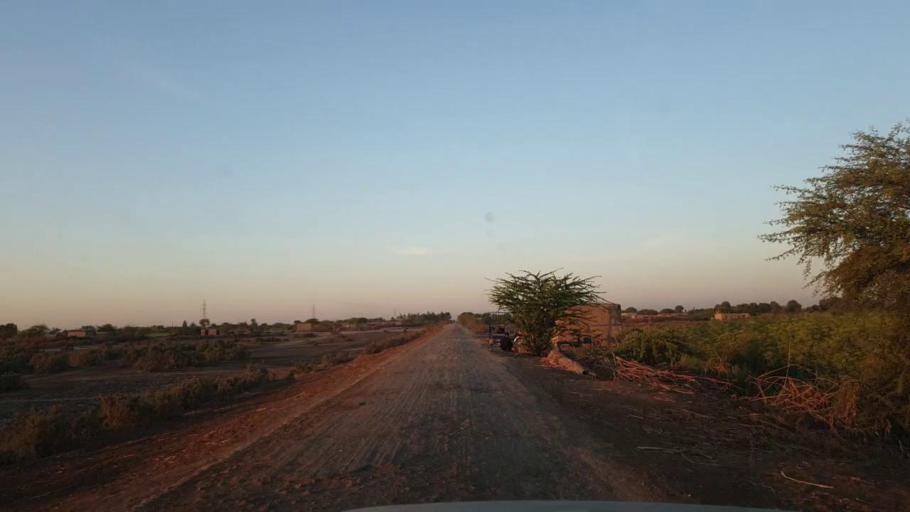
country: PK
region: Sindh
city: Kunri
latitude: 25.1413
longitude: 69.4447
